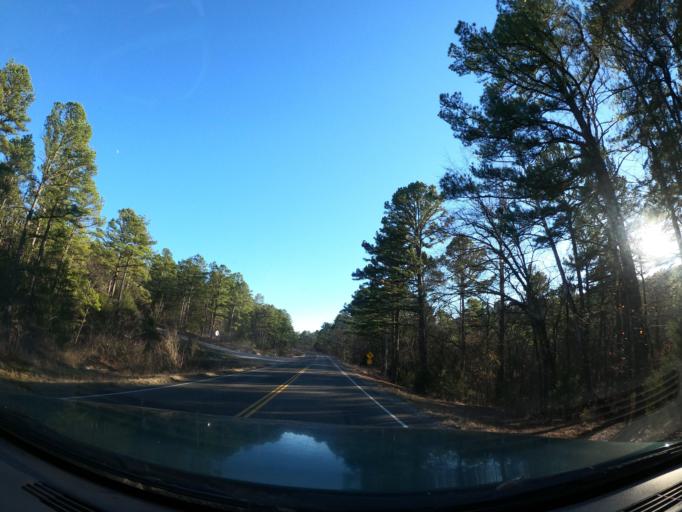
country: US
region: Oklahoma
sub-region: Latimer County
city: Wilburton
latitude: 34.9654
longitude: -95.3573
